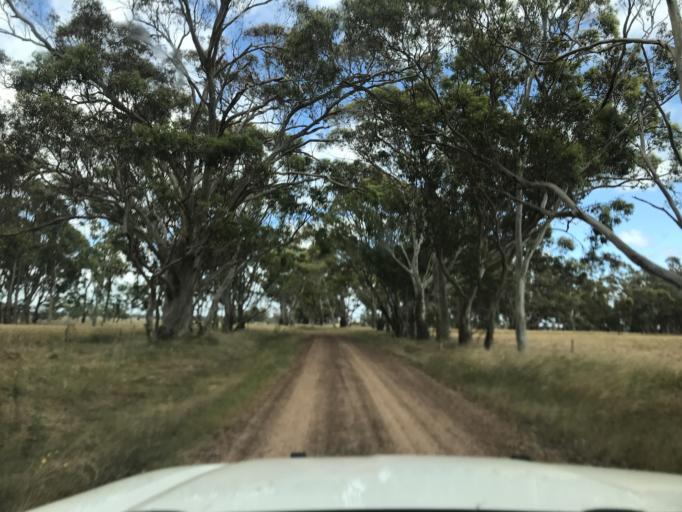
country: AU
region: South Australia
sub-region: Naracoorte and Lucindale
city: Naracoorte
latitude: -36.8994
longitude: 141.3912
